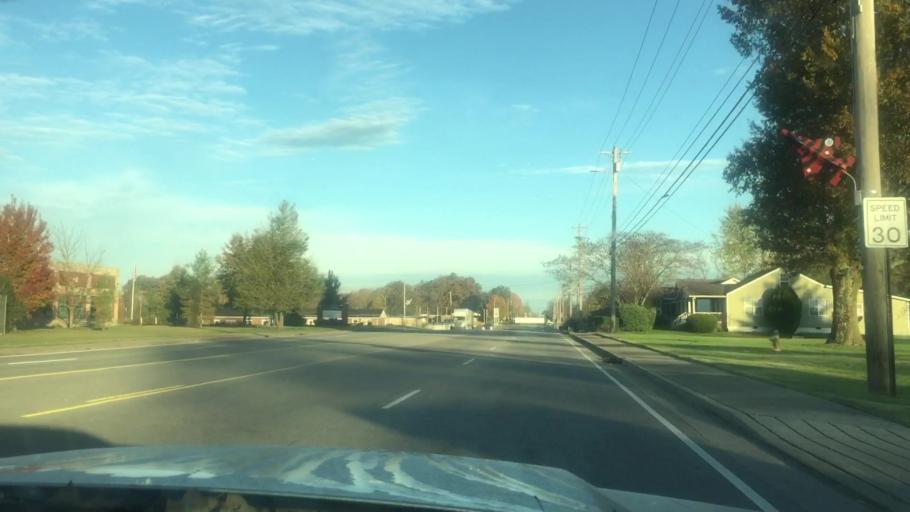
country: US
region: Tennessee
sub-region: Coffee County
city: Tullahoma
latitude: 35.3523
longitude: -86.2028
